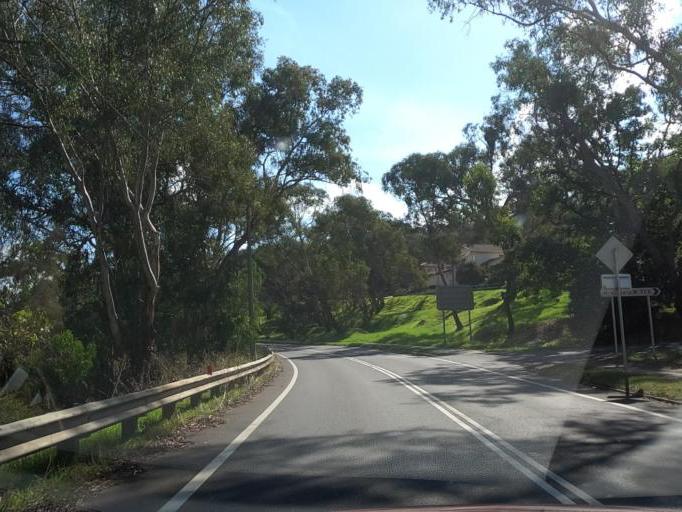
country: AU
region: New South Wales
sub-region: Albury Municipality
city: South Albury
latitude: -36.0820
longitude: 146.9057
